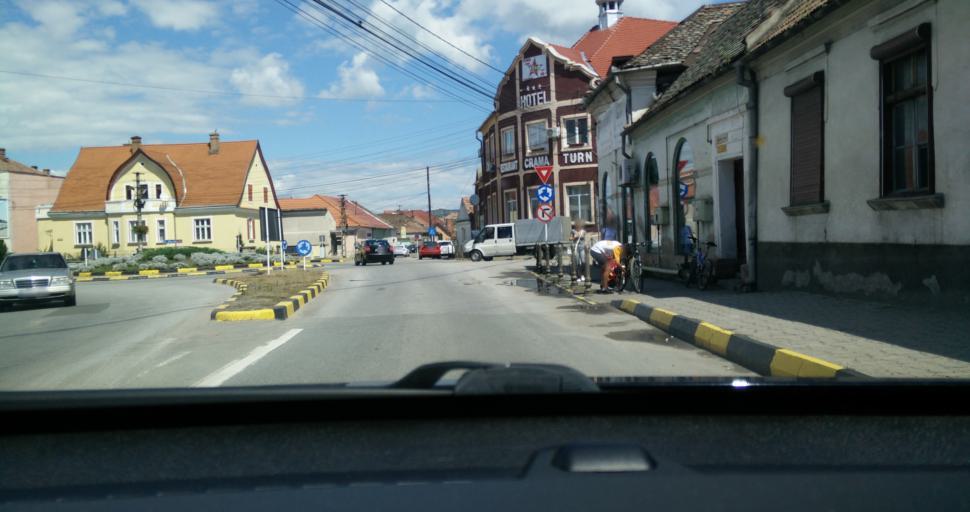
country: RO
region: Alba
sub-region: Municipiul Sebes
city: Sebes
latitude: 45.9575
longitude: 23.5655
